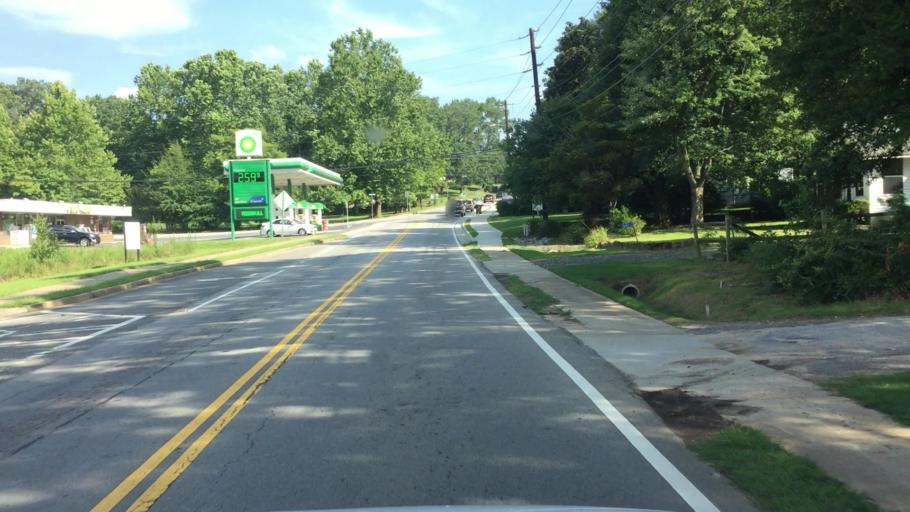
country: US
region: Georgia
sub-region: Gwinnett County
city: Dacula
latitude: 33.9869
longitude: -83.8935
